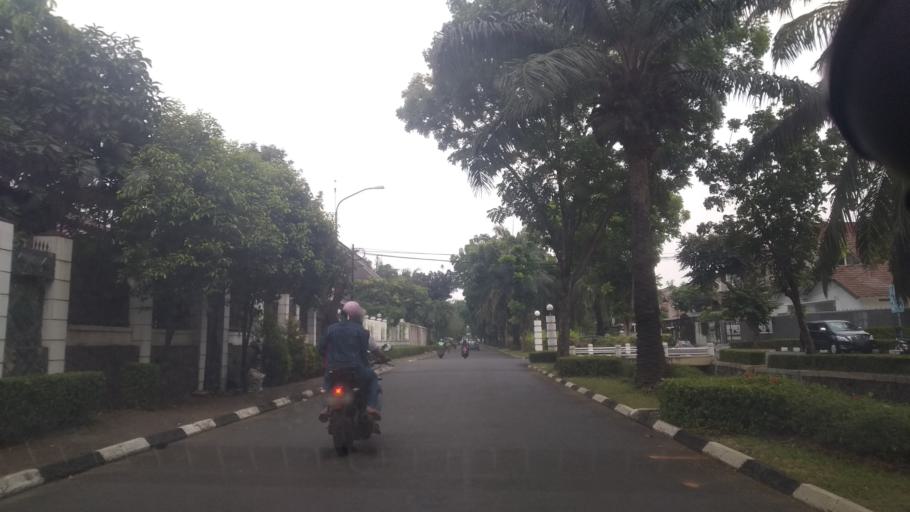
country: ID
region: Banten
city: South Tangerang
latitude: -6.2693
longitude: 106.7467
